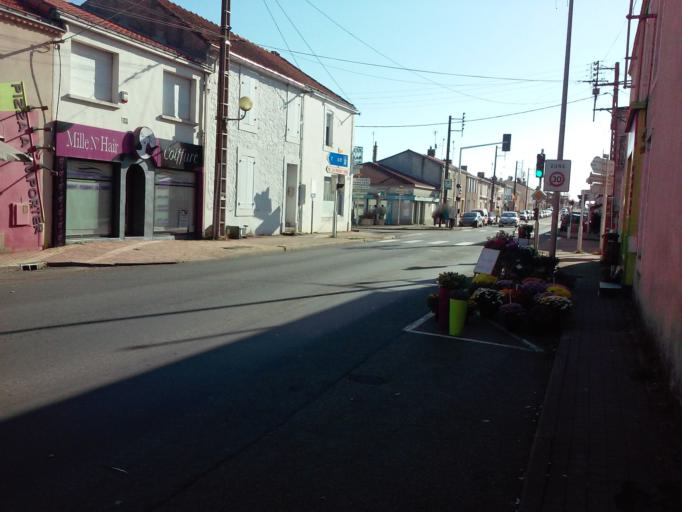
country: FR
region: Pays de la Loire
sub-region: Departement de la Vendee
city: Saint-Florent-des-Bois
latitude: 46.5937
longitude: -1.3162
